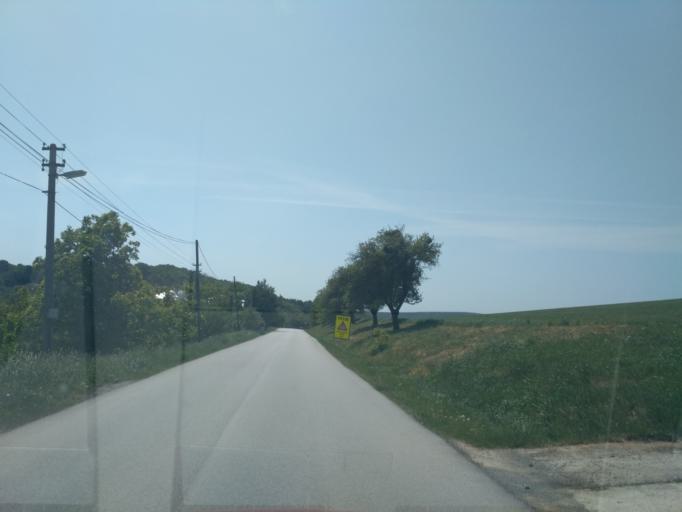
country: SK
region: Kosicky
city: Kosice
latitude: 48.7906
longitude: 21.3460
